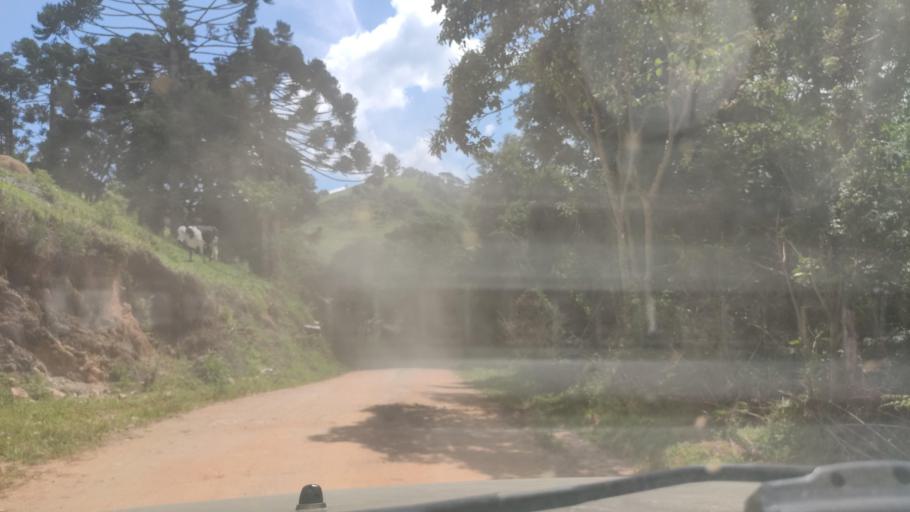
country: BR
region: Minas Gerais
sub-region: Cambui
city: Cambui
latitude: -22.6950
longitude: -45.9872
